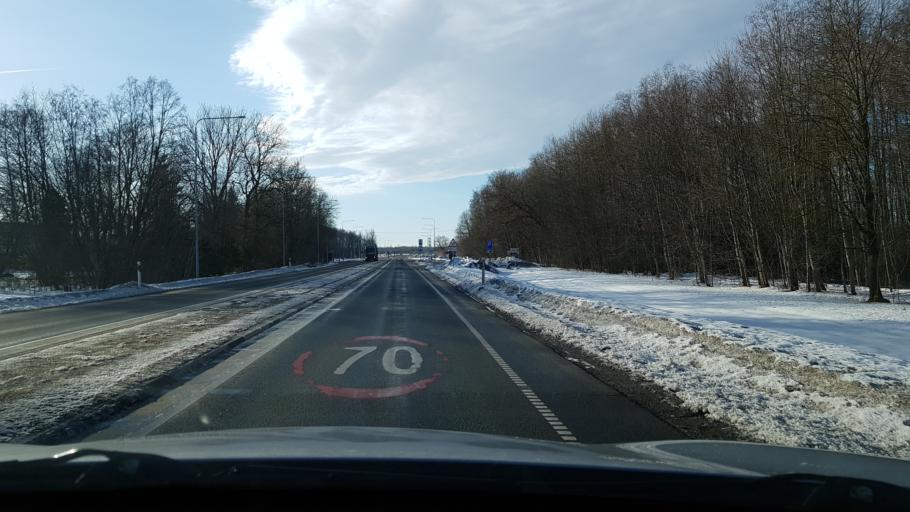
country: EE
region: Viljandimaa
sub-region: Vohma linn
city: Vohma
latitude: 58.6313
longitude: 25.5717
